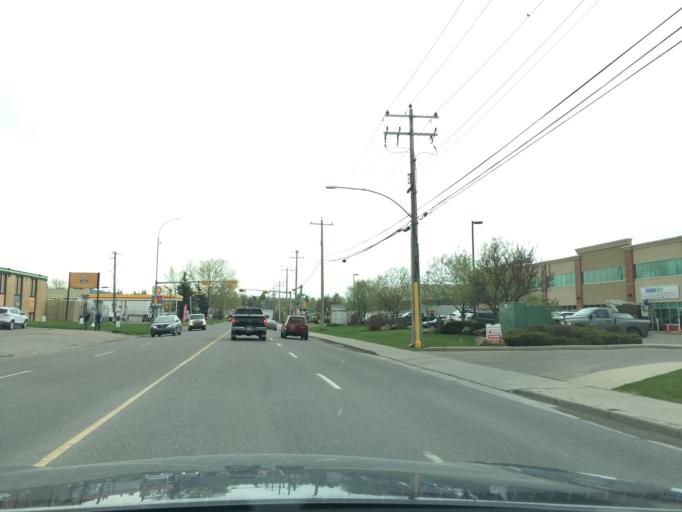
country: CA
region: Alberta
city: Calgary
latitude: 50.9929
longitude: -114.0638
